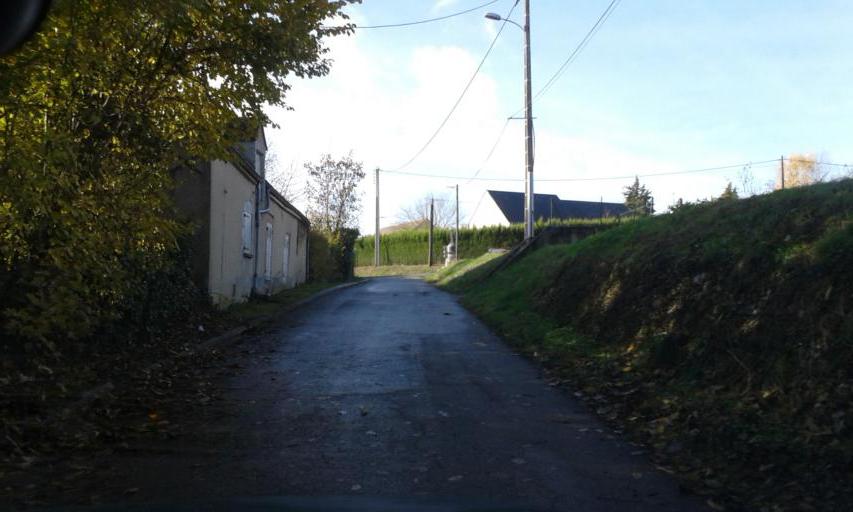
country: FR
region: Centre
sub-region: Departement du Loir-et-Cher
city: Mer
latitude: 47.7104
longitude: 1.5416
